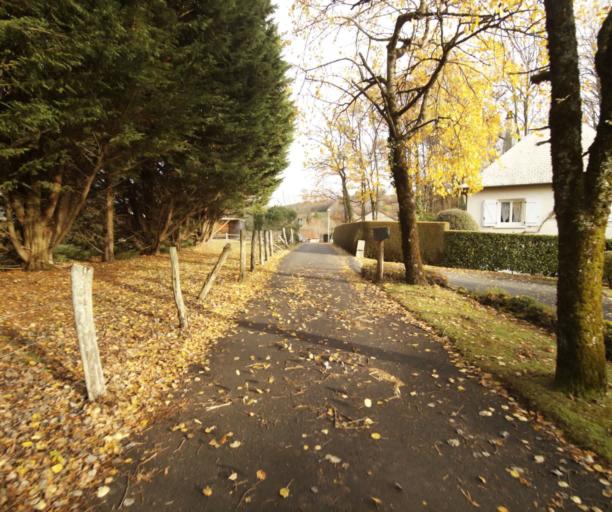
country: FR
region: Limousin
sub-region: Departement de la Correze
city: Sainte-Fortunade
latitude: 45.2038
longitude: 1.7697
